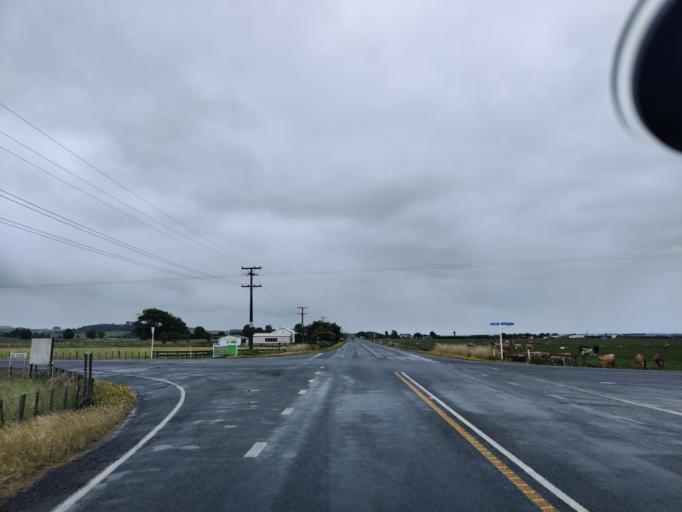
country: NZ
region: Northland
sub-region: Kaipara District
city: Dargaville
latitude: -35.9517
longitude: 173.8924
